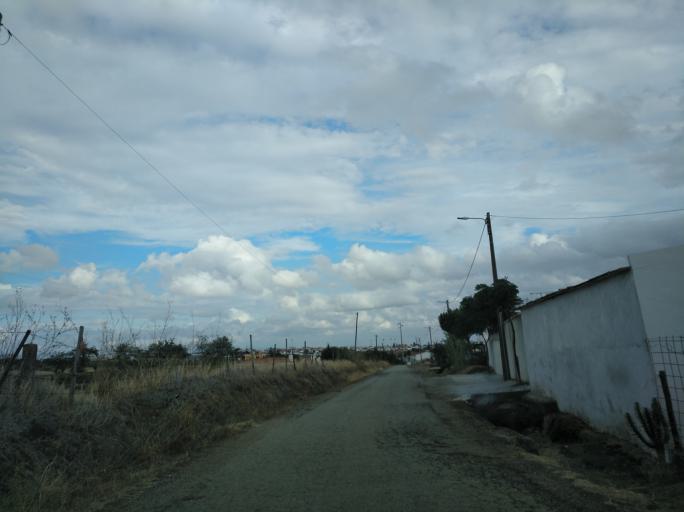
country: PT
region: Portalegre
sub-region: Campo Maior
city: Campo Maior
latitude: 39.0207
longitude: -7.0804
